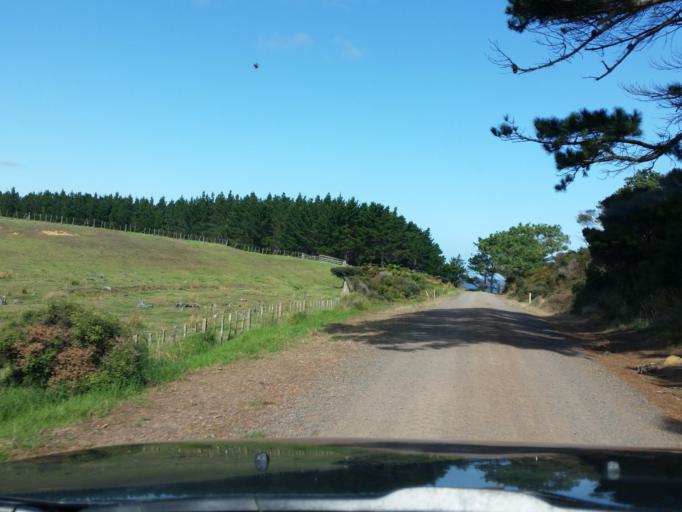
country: NZ
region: Northland
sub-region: Kaipara District
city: Dargaville
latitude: -35.7001
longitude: 173.5227
